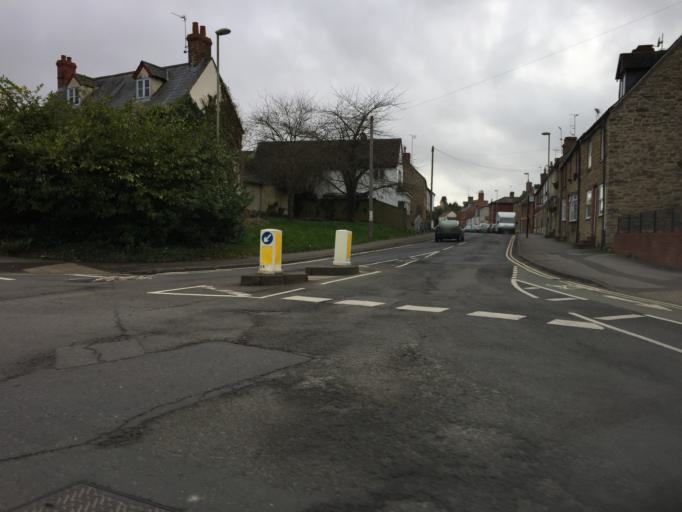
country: GB
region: England
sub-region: Oxfordshire
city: Faringdon
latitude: 51.6564
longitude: -1.5870
